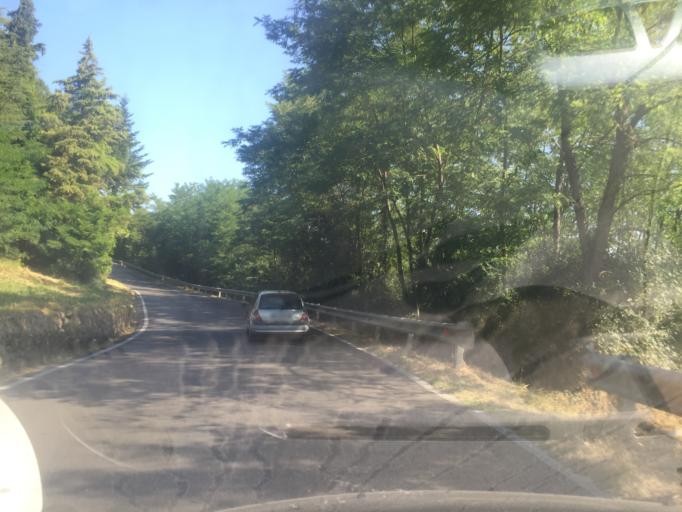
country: IT
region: Tuscany
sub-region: Provincia di Lucca
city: Castelnuovo di Garfagnana
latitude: 44.1207
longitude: 10.3939
